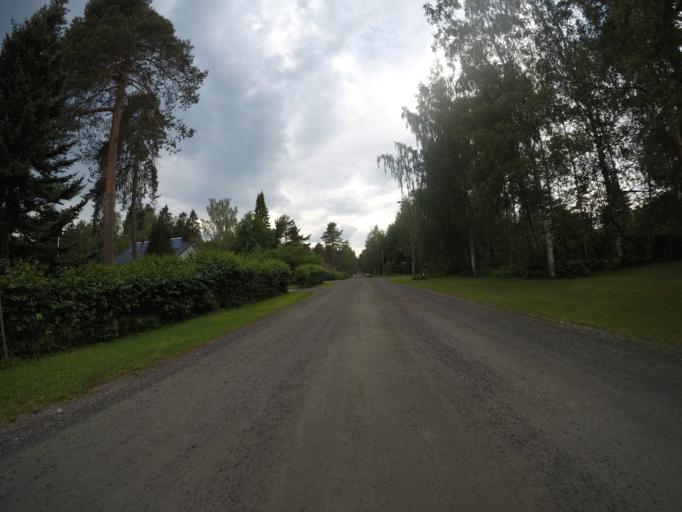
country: FI
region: Haeme
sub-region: Haemeenlinna
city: Haemeenlinna
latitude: 61.0110
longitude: 24.4928
